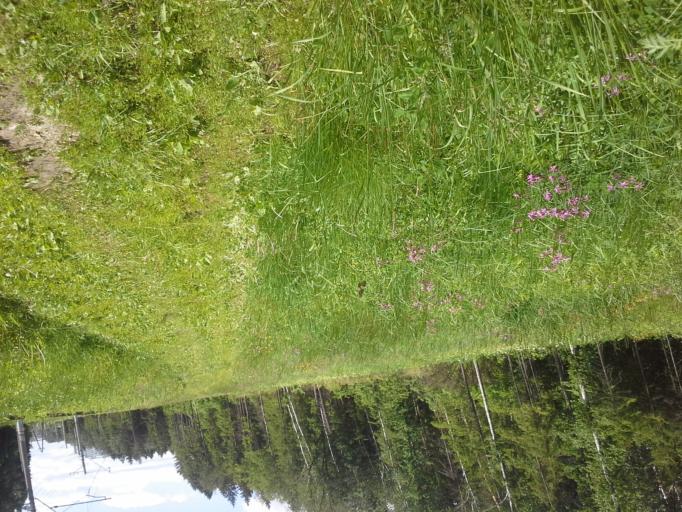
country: RU
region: Moscow
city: Tolstopal'tsevo
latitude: 55.6196
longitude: 37.2398
